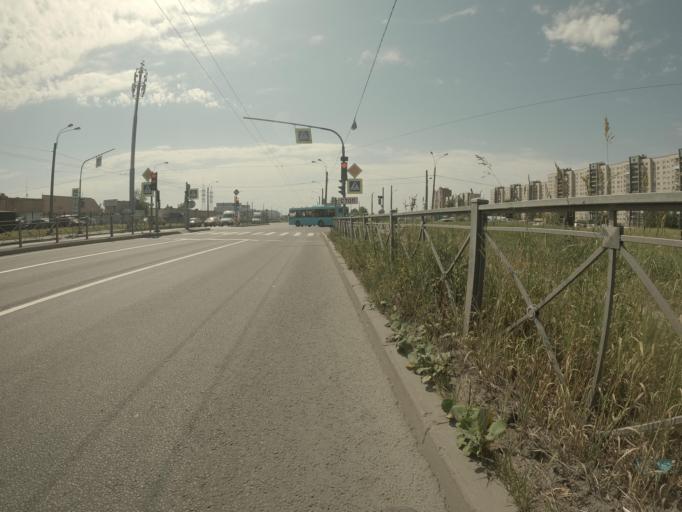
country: RU
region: St.-Petersburg
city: Krasnogvargeisky
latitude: 59.9397
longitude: 30.5041
